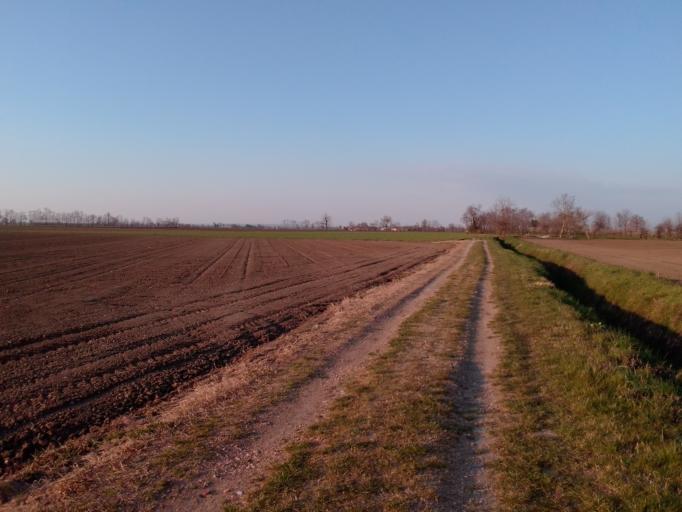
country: IT
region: Emilia-Romagna
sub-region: Provincia di Piacenza
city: Borgonovo Valtidone
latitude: 44.9969
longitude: 9.4813
